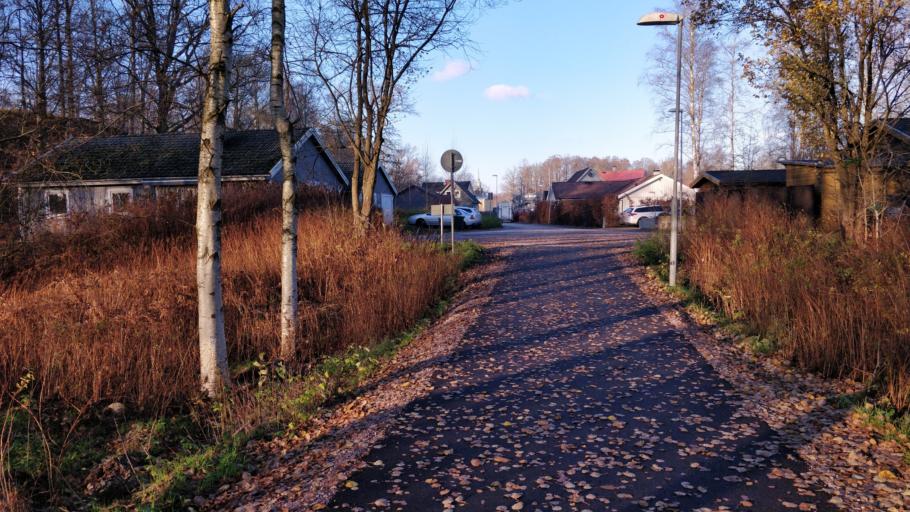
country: SE
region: Kronoberg
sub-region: Almhults Kommun
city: AElmhult
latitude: 56.5461
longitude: 14.1308
